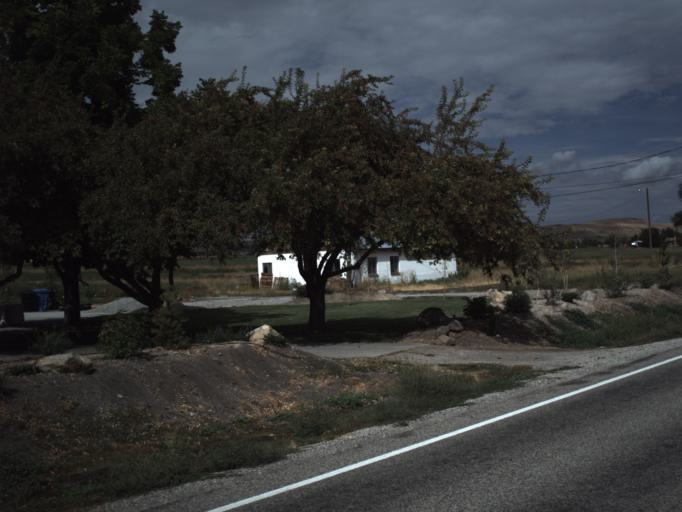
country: US
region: Utah
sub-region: Cache County
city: Mendon
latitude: 41.7307
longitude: -111.9791
